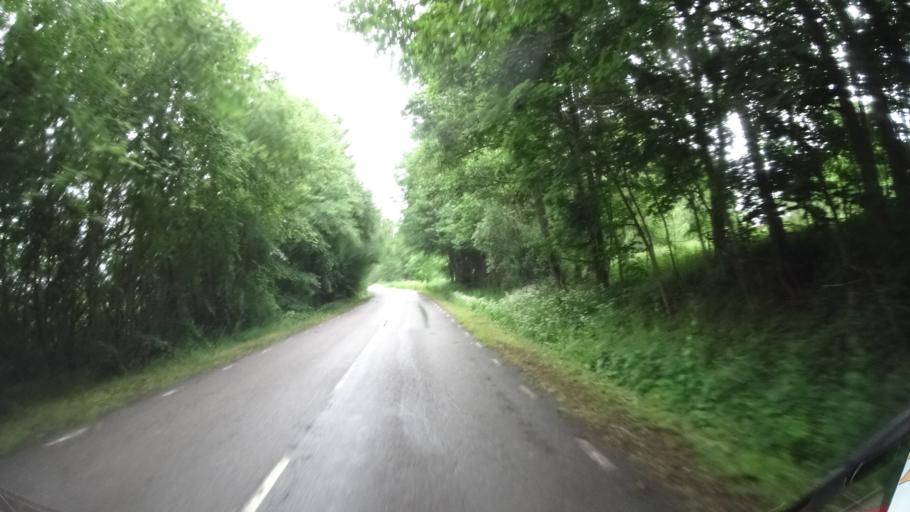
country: SE
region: Kalmar
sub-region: Vasterviks Kommun
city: Vaestervik
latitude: 57.8178
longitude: 16.5769
